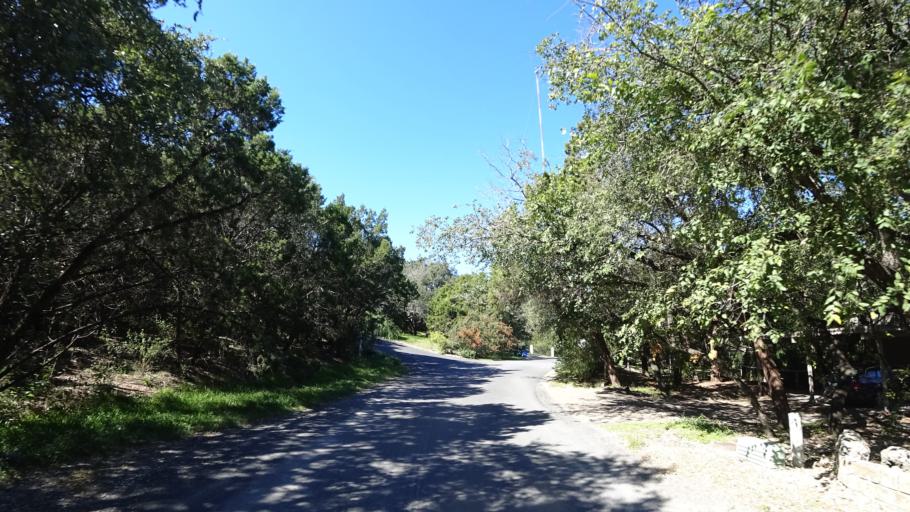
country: US
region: Texas
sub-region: Travis County
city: West Lake Hills
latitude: 30.3193
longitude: -97.7980
